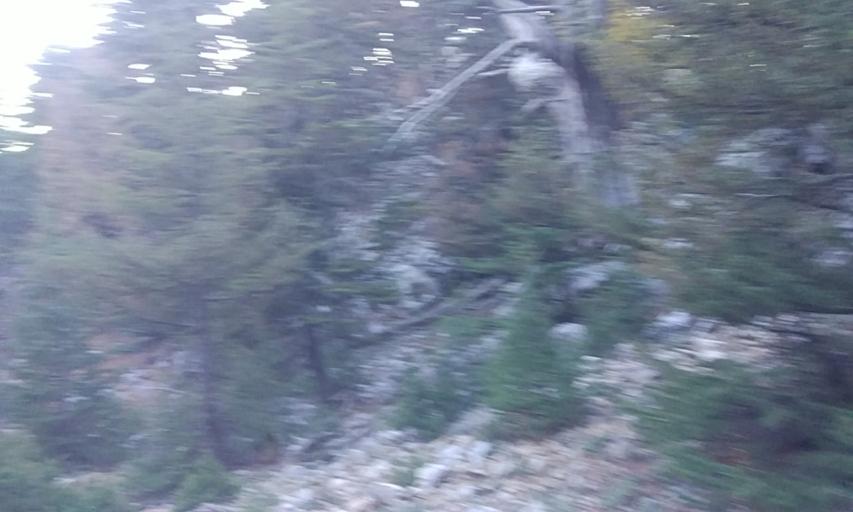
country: TR
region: Antalya
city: Altinyaka
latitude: 36.5376
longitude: 30.4172
